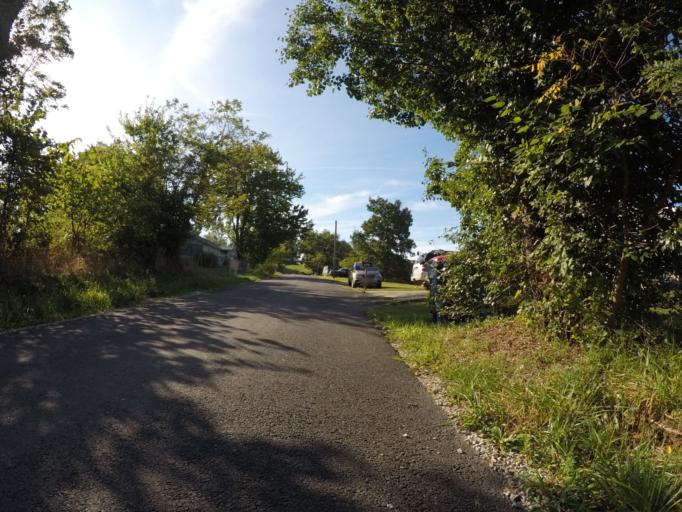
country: US
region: Ohio
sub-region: Lawrence County
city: Burlington
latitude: 38.5254
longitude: -82.5252
